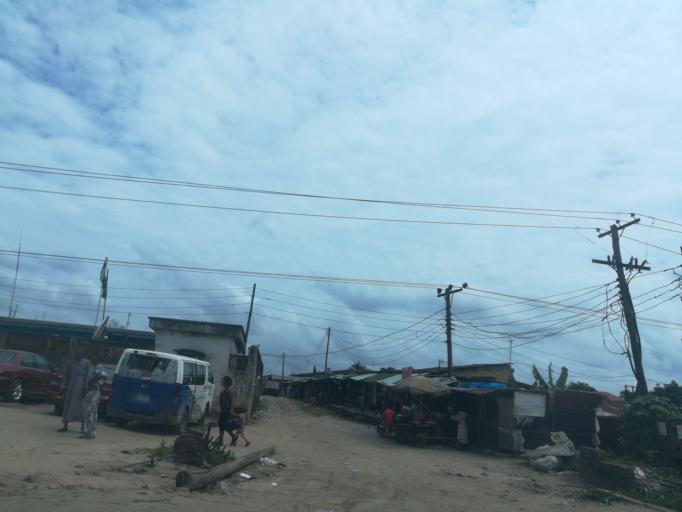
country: NG
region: Lagos
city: Ikotun
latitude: 6.4957
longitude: 3.1254
